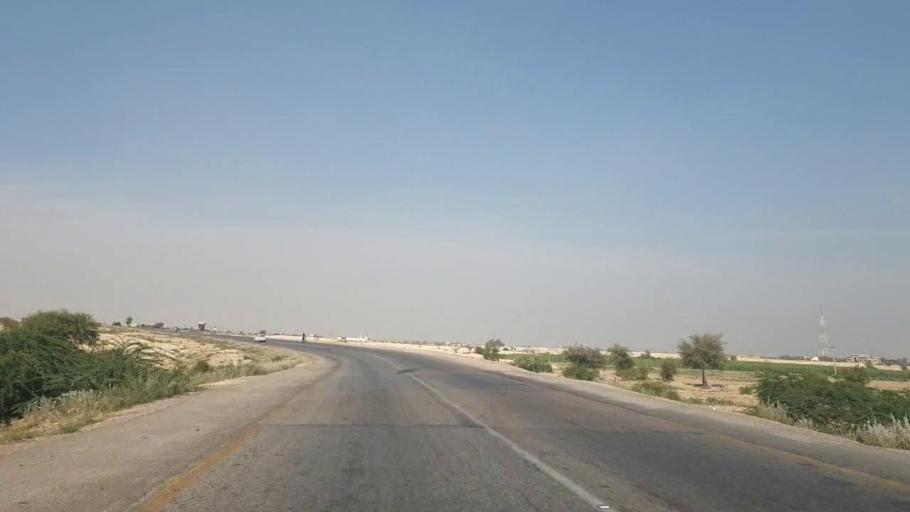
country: PK
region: Sindh
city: Hala
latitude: 25.7971
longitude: 68.2802
